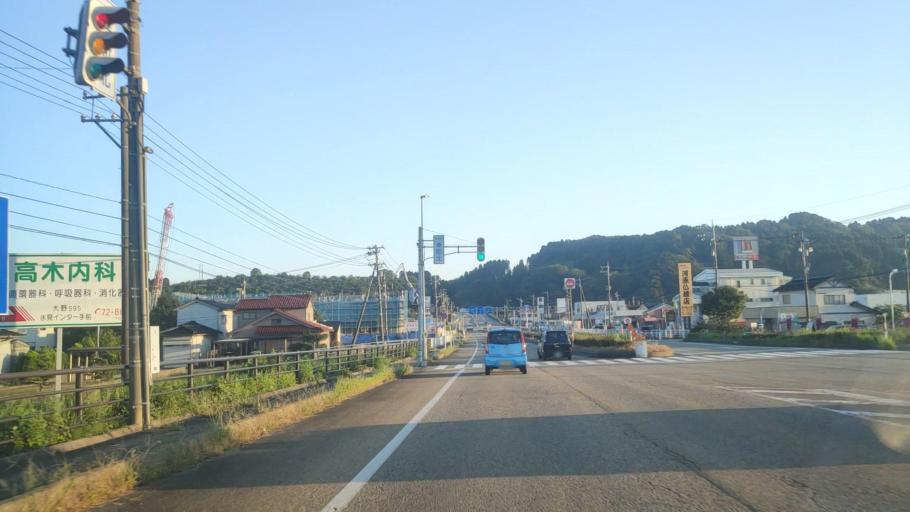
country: JP
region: Toyama
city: Himi
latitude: 36.8606
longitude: 136.9758
